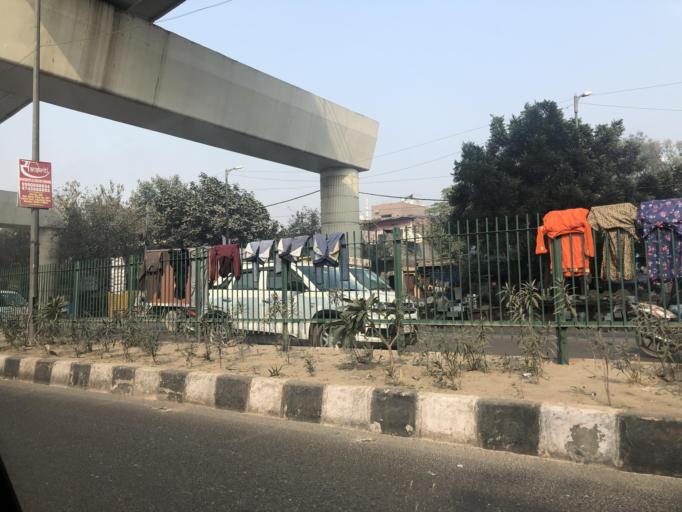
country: IN
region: NCT
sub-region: West Delhi
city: Nangloi Jat
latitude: 28.6820
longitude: 77.0727
